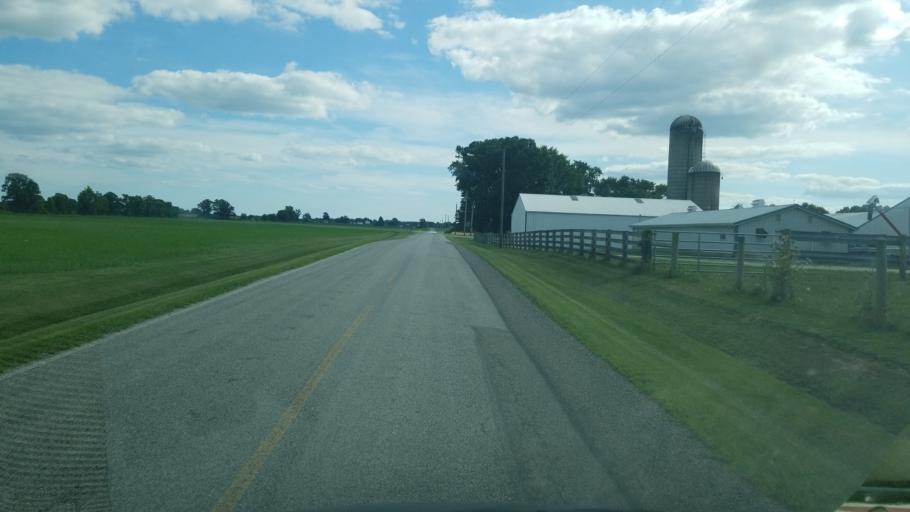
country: US
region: Ohio
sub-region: Champaign County
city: Saint Paris
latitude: 40.2061
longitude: -83.9424
